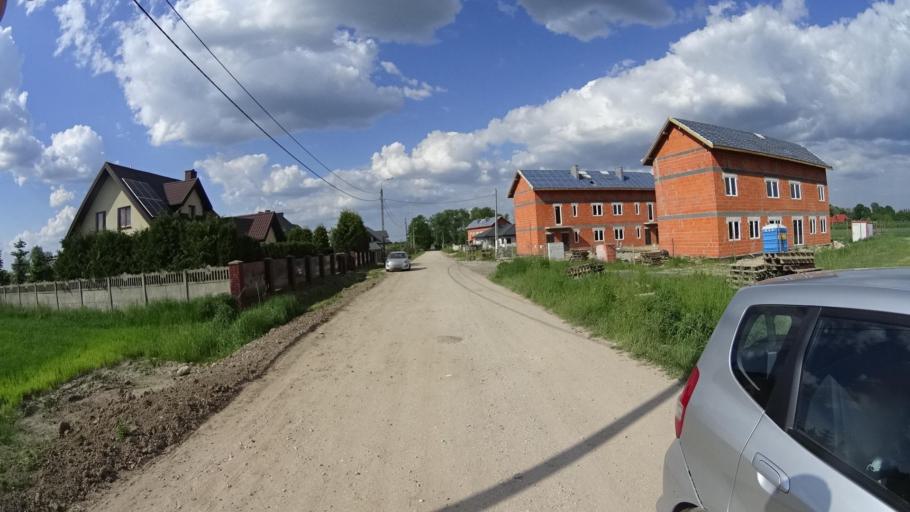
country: PL
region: Masovian Voivodeship
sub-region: Powiat piaseczynski
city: Tarczyn
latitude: 52.0304
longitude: 20.8209
